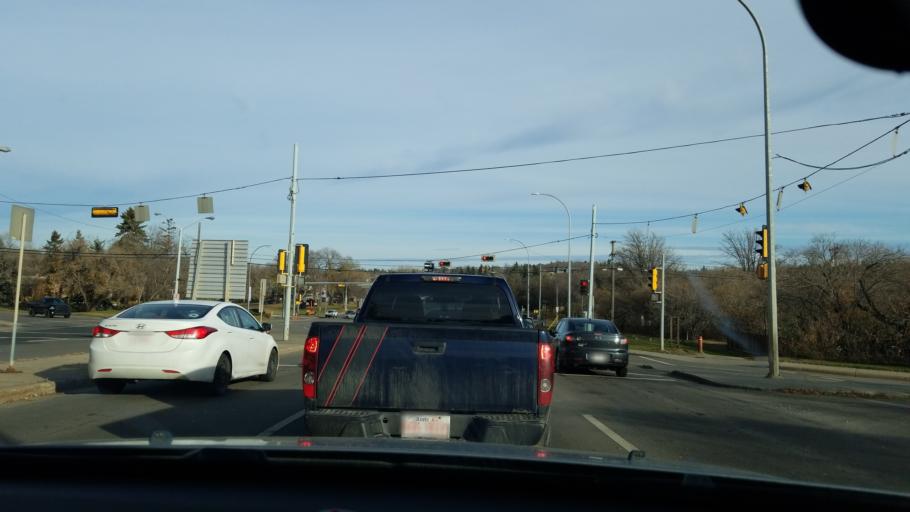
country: CA
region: Alberta
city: Edmonton
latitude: 53.5339
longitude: -113.4994
